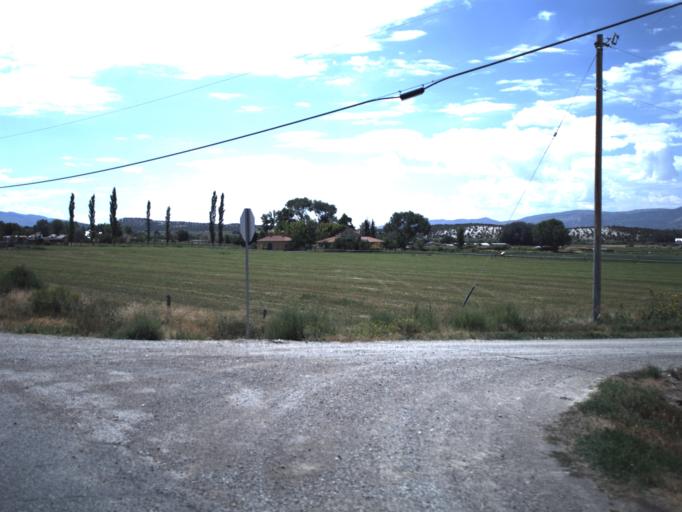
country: US
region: Utah
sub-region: Sanpete County
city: Mount Pleasant
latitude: 39.4884
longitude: -111.4961
